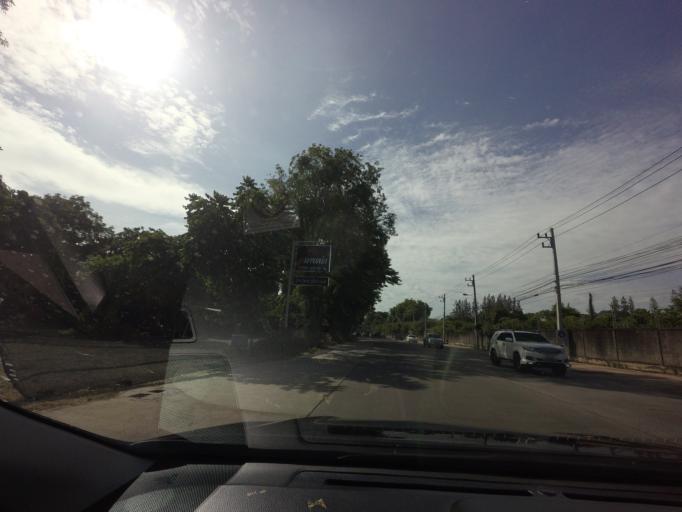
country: TH
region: Chon Buri
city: Si Racha
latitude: 13.1591
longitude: 100.9407
